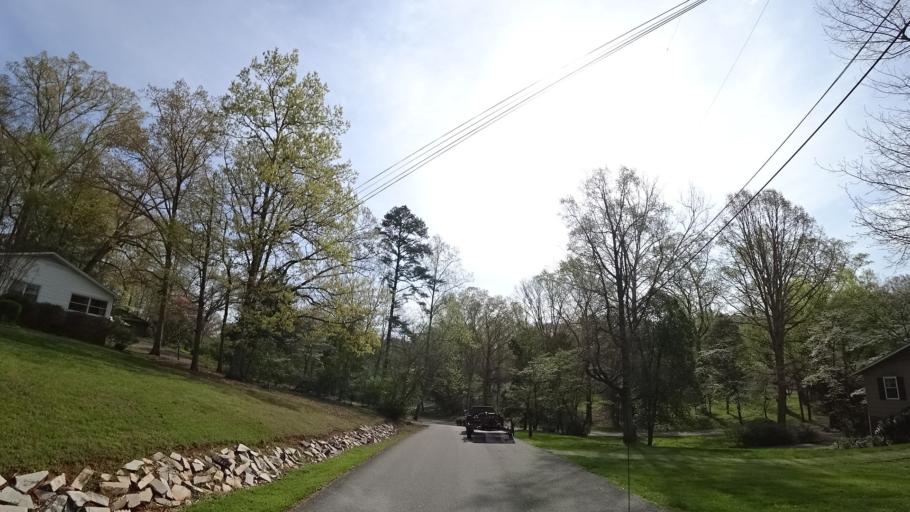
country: US
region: Tennessee
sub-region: Knox County
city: Knoxville
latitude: 35.8999
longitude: -83.9843
